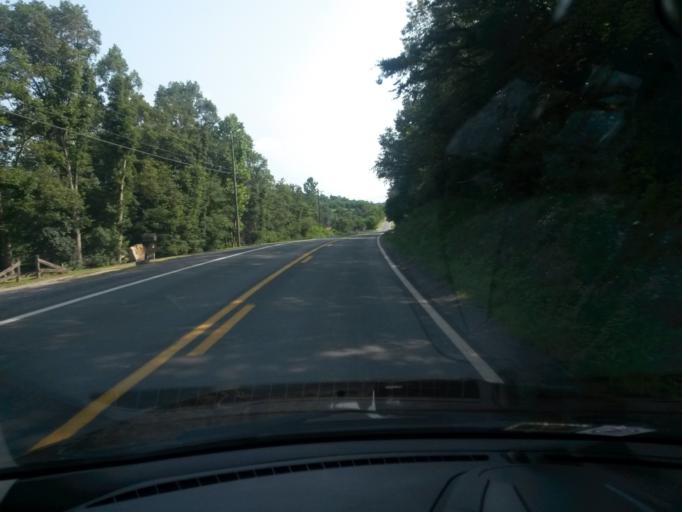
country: US
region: Virginia
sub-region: Shenandoah County
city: Basye
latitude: 38.8390
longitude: -78.8769
